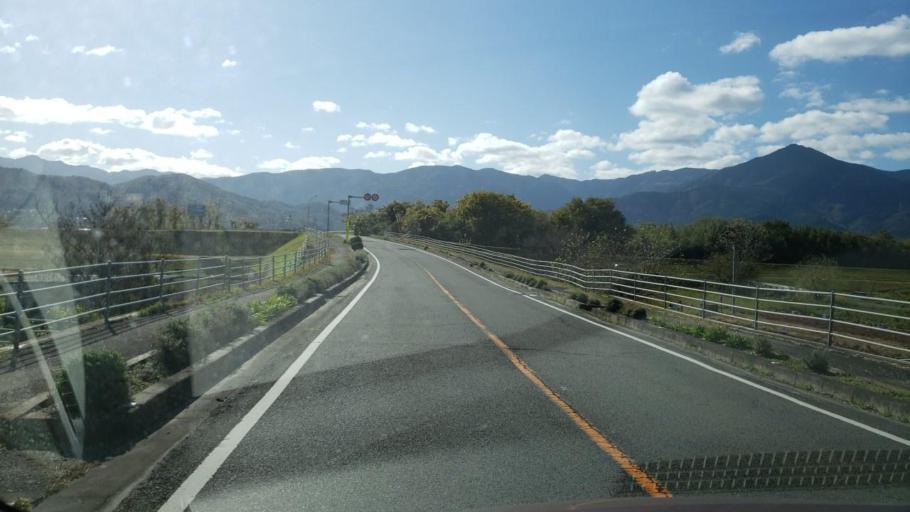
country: JP
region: Tokushima
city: Wakimachi
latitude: 34.0736
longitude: 134.2364
